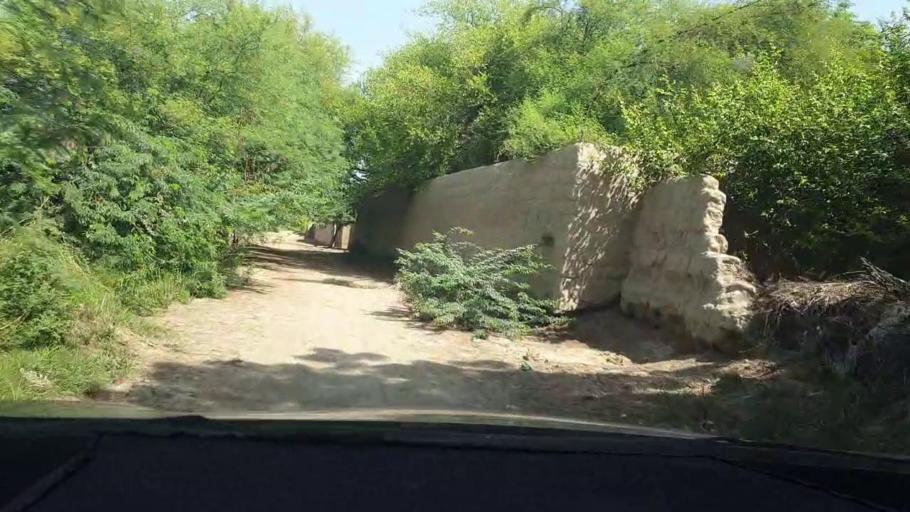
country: PK
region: Sindh
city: Kambar
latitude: 27.6004
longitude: 68.0638
